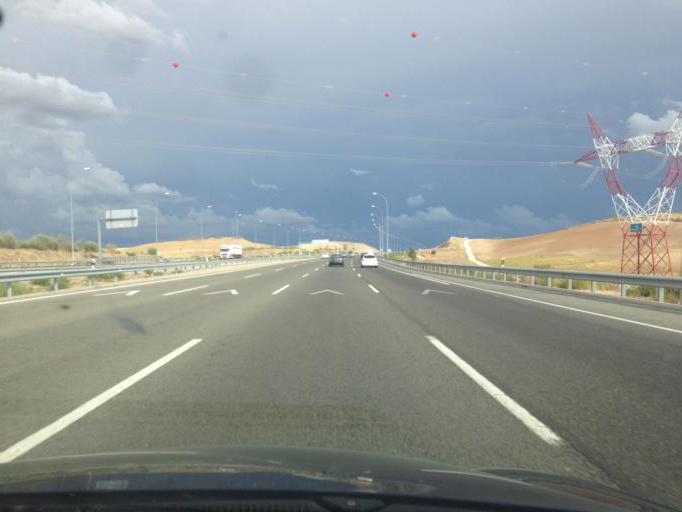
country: ES
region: Madrid
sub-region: Provincia de Madrid
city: Paracuellos de Jarama
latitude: 40.5391
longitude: -3.5301
